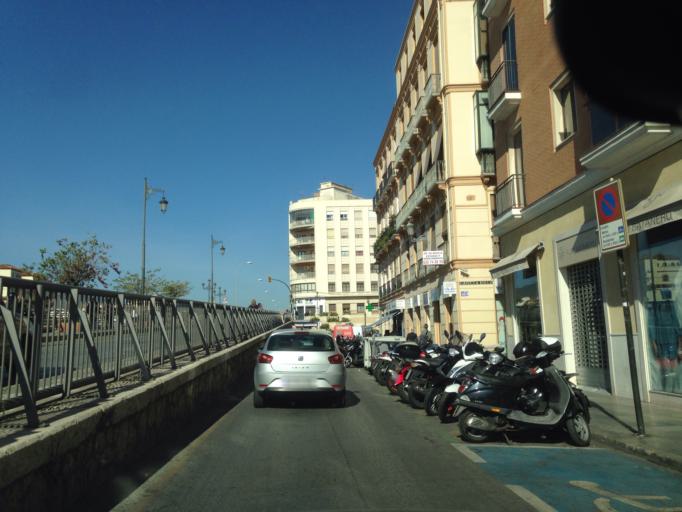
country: ES
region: Andalusia
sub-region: Provincia de Malaga
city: Malaga
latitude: 36.7208
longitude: -4.4251
